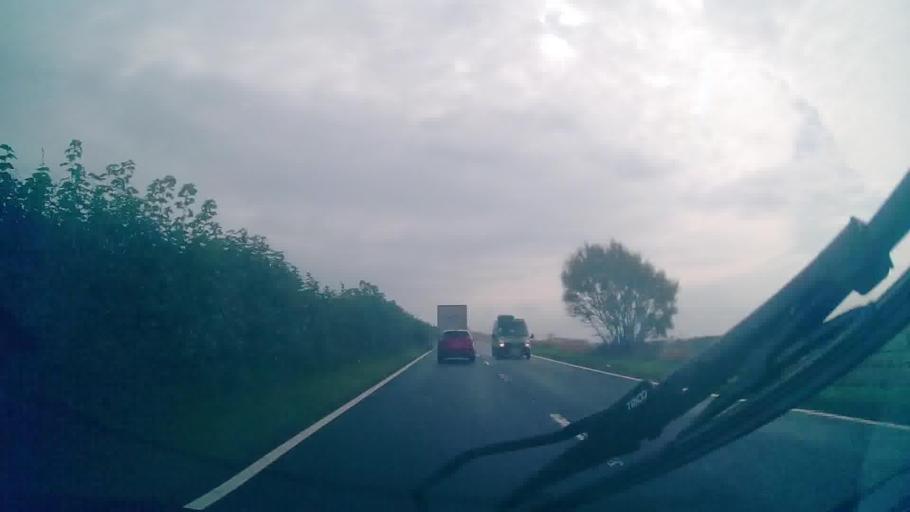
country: GB
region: Scotland
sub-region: Dumfries and Galloway
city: Lochmaben
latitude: 55.0569
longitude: -3.4728
